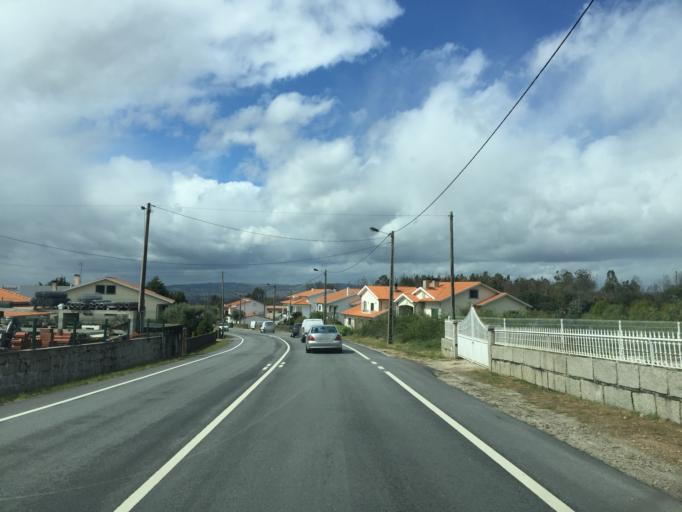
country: PT
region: Guarda
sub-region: Manteigas
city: Manteigas
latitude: 40.5052
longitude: -7.6155
